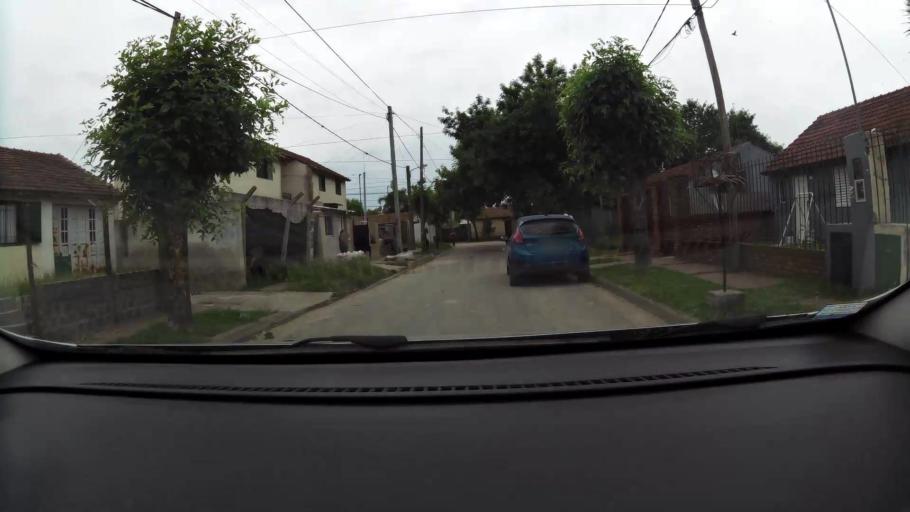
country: AR
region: Buenos Aires
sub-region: Partido de Campana
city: Campana
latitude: -34.2110
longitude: -58.9438
